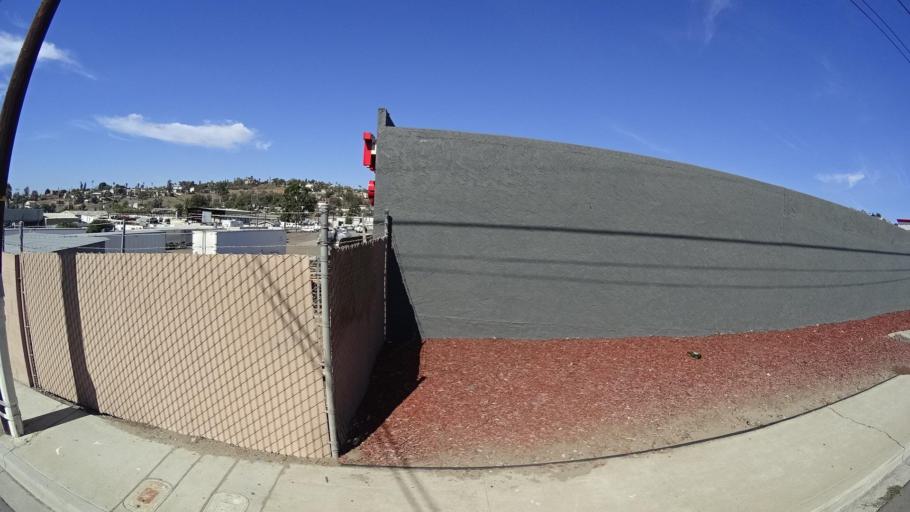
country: US
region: California
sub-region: San Diego County
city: La Presa
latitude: 32.7150
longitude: -117.0028
